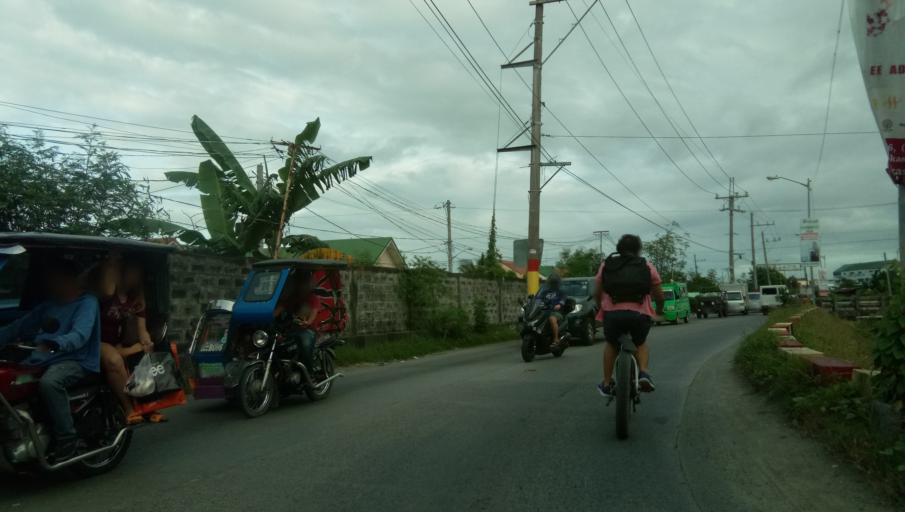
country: PH
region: Calabarzon
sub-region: Province of Cavite
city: Dasmarinas
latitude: 14.3679
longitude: 120.9275
